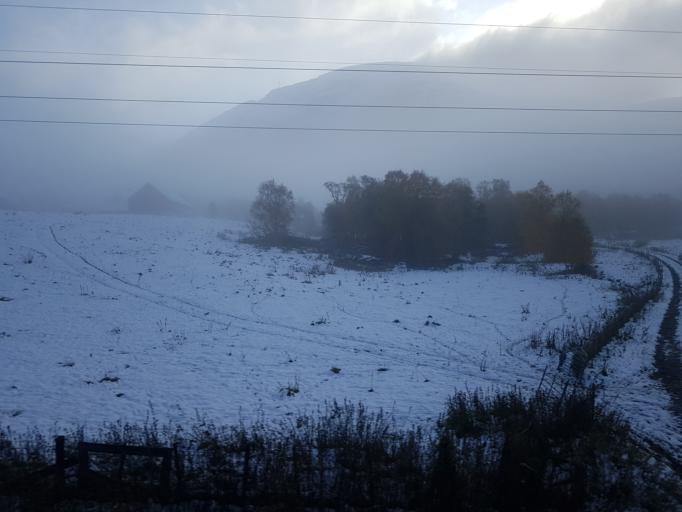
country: NO
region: Sor-Trondelag
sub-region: Oppdal
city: Oppdal
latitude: 62.5689
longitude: 9.6463
